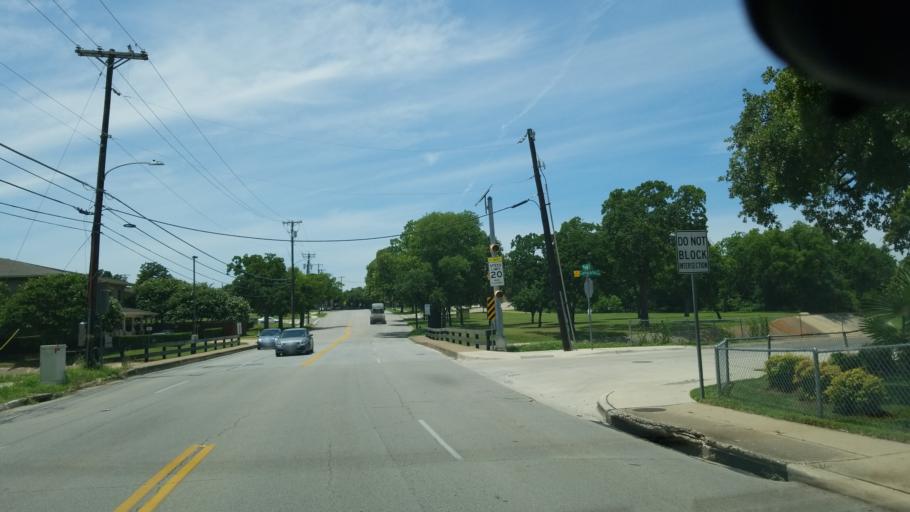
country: US
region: Texas
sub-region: Dallas County
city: Irving
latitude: 32.8182
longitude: -96.9519
